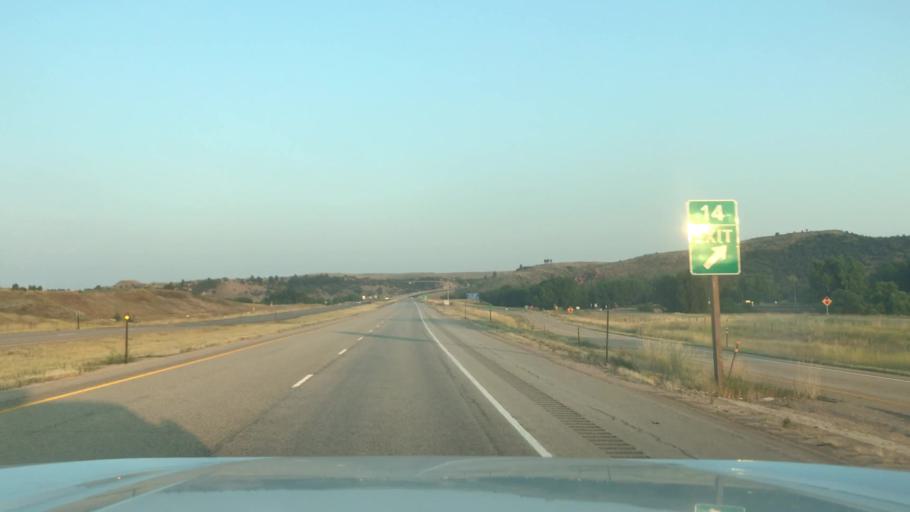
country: US
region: Wyoming
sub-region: Sheridan County
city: Sheridan
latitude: 44.9056
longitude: -107.0300
